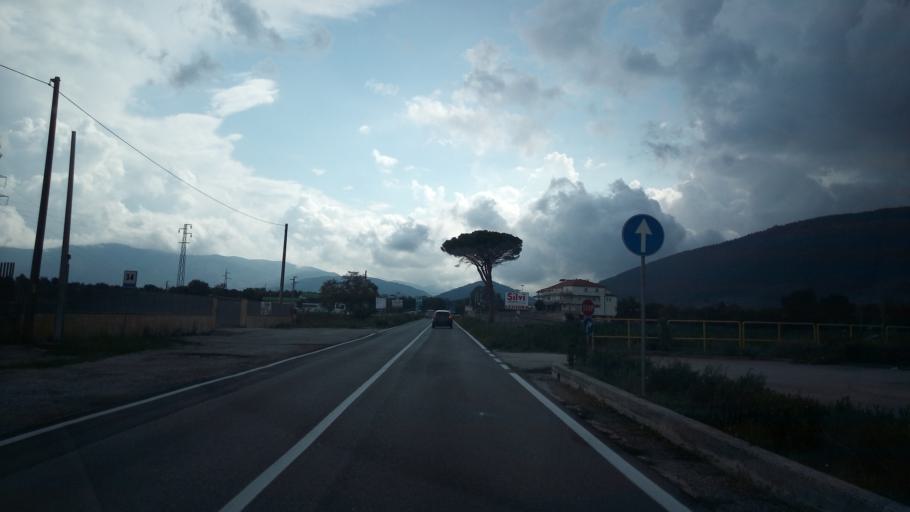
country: IT
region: Campania
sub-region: Provincia di Salerno
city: Buonabitacolo
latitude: 40.2902
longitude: 15.6415
